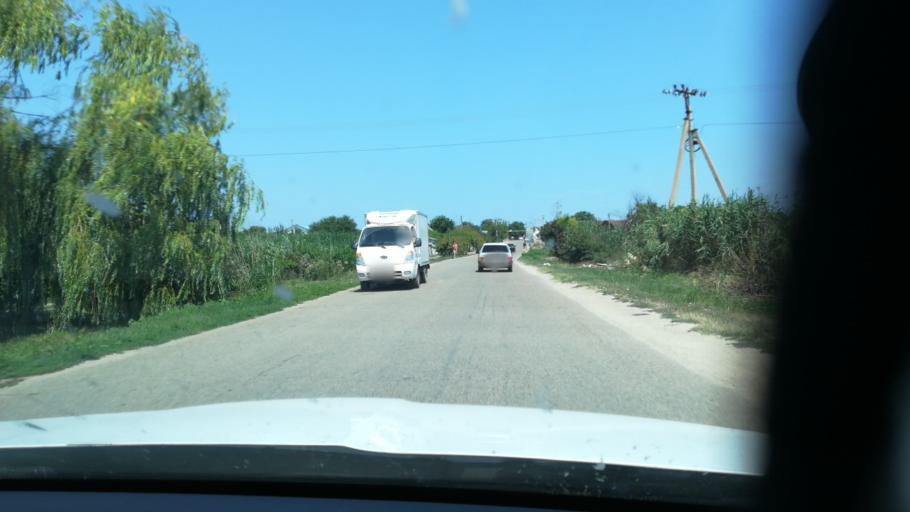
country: RU
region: Krasnodarskiy
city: Starotitarovskaya
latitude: 45.2105
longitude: 37.1450
